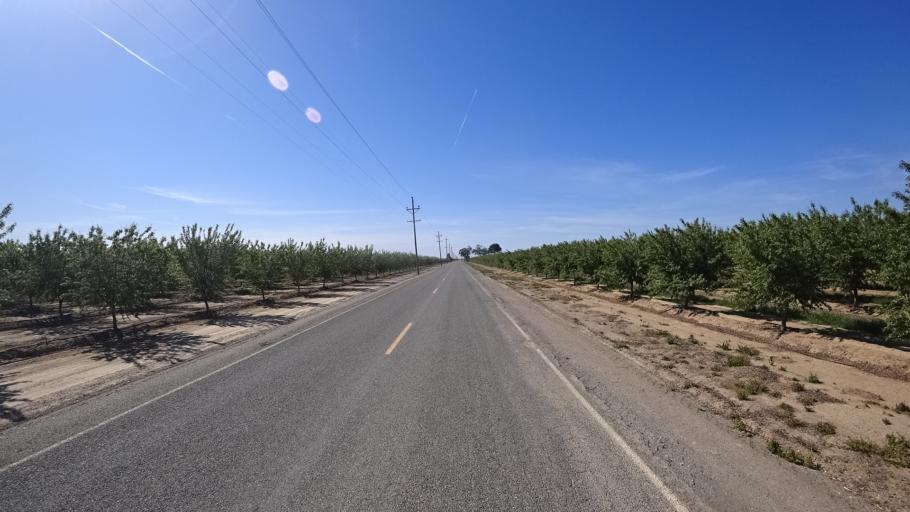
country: US
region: California
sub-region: Glenn County
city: Orland
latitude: 39.6442
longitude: -122.1787
